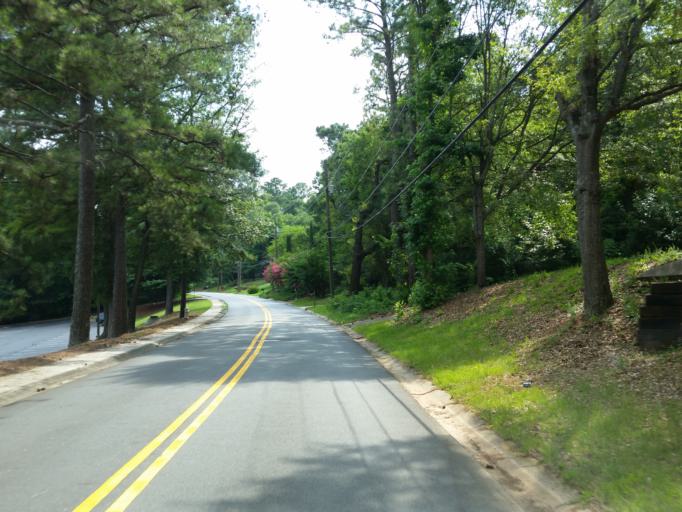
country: US
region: Georgia
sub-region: Cobb County
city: Marietta
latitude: 33.9583
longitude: -84.5300
